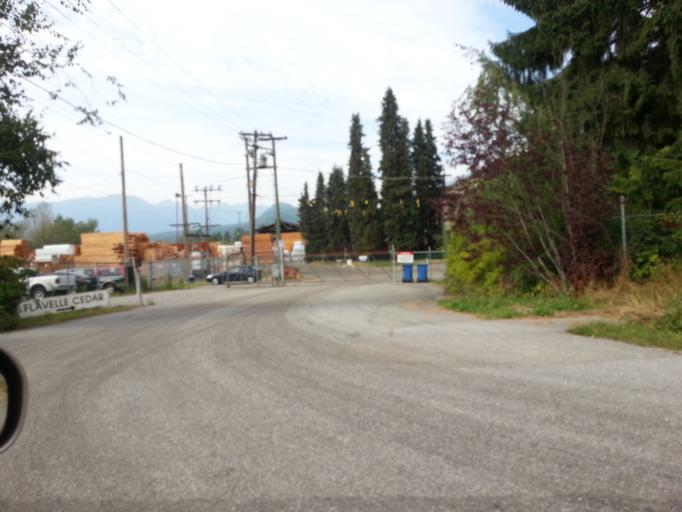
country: CA
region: British Columbia
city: Port Moody
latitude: 49.2784
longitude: -122.8565
